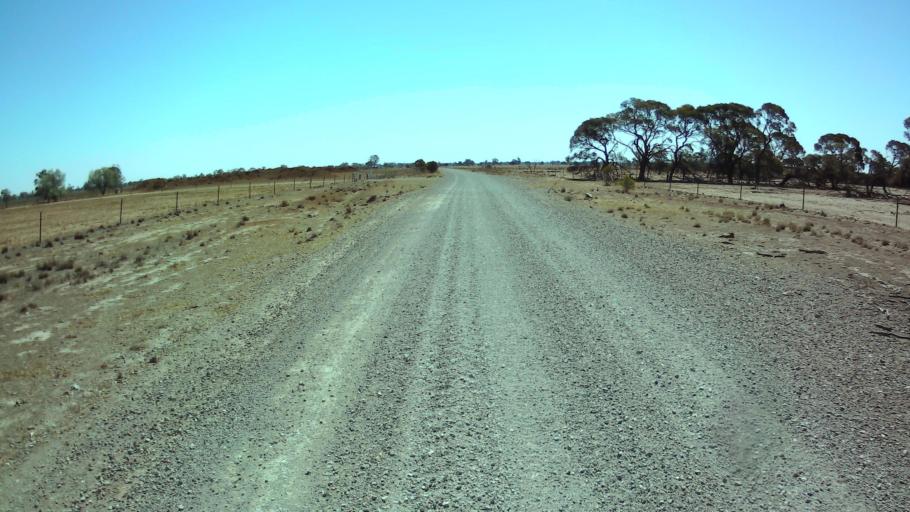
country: AU
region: New South Wales
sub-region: Forbes
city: Forbes
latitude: -33.7455
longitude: 147.7364
